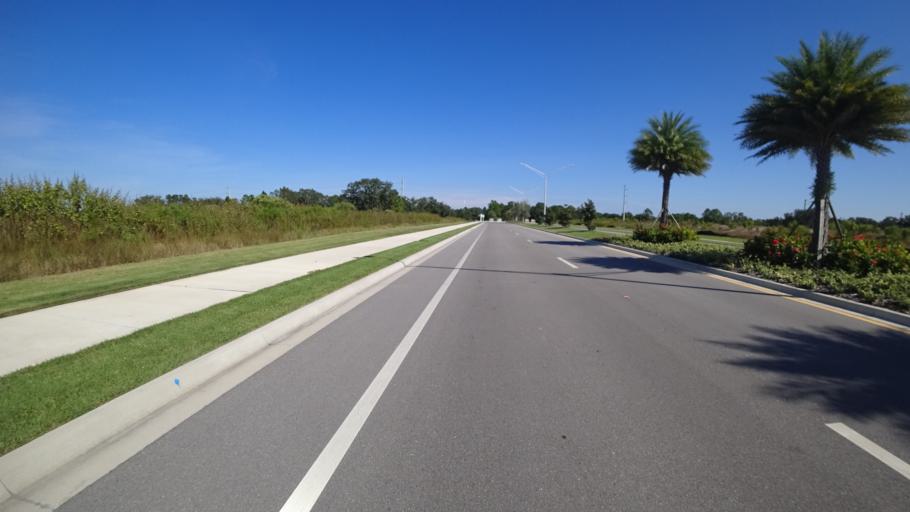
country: US
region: Florida
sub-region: Sarasota County
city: The Meadows
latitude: 27.4027
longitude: -82.3562
